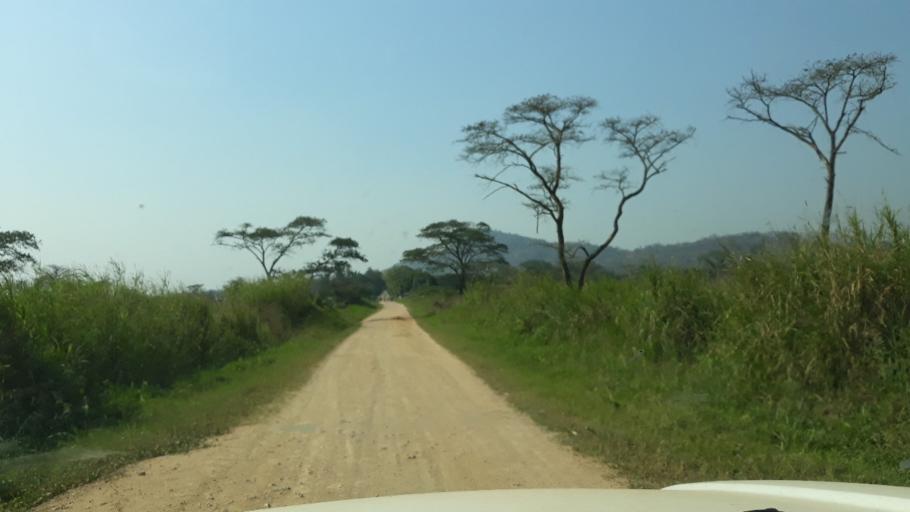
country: TZ
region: Kigoma
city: Kigoma
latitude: -4.6267
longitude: 28.7781
